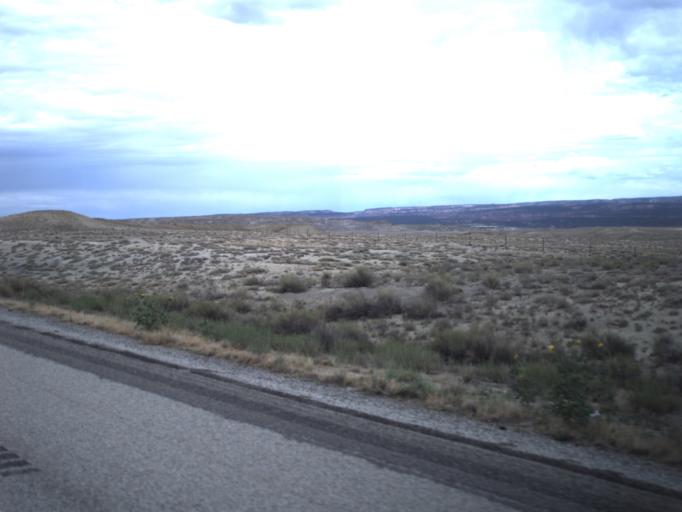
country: US
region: Utah
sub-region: Grand County
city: Moab
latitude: 38.9935
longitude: -109.3300
